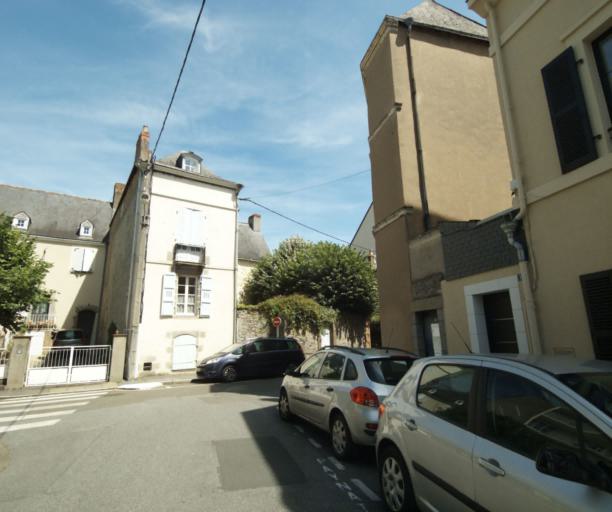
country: FR
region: Pays de la Loire
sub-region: Departement de la Mayenne
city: Laval
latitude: 48.0723
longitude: -0.7670
